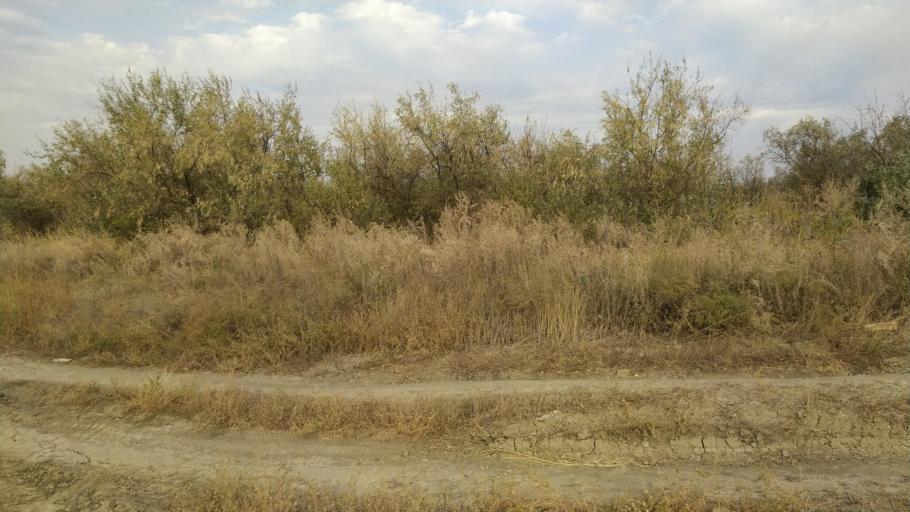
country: RU
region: Rostov
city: Kuleshovka
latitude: 47.1168
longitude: 39.6013
